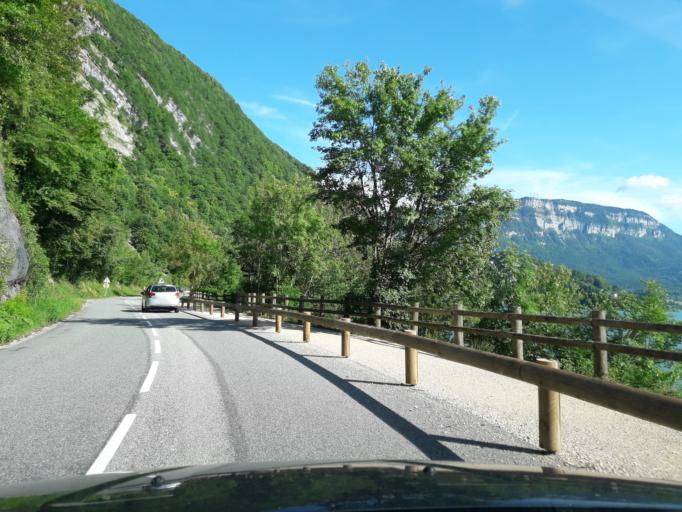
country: FR
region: Rhone-Alpes
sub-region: Departement de la Savoie
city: Novalaise
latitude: 45.5733
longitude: 5.8065
